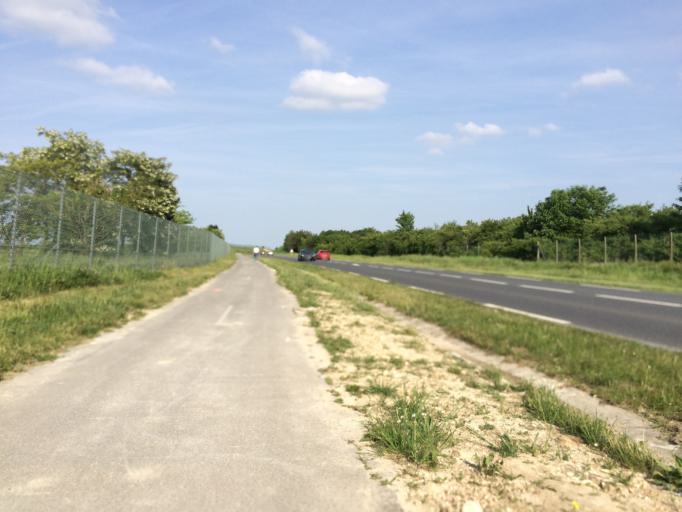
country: FR
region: Ile-de-France
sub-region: Departement de l'Essonne
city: Morangis
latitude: 48.7135
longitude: 2.3434
